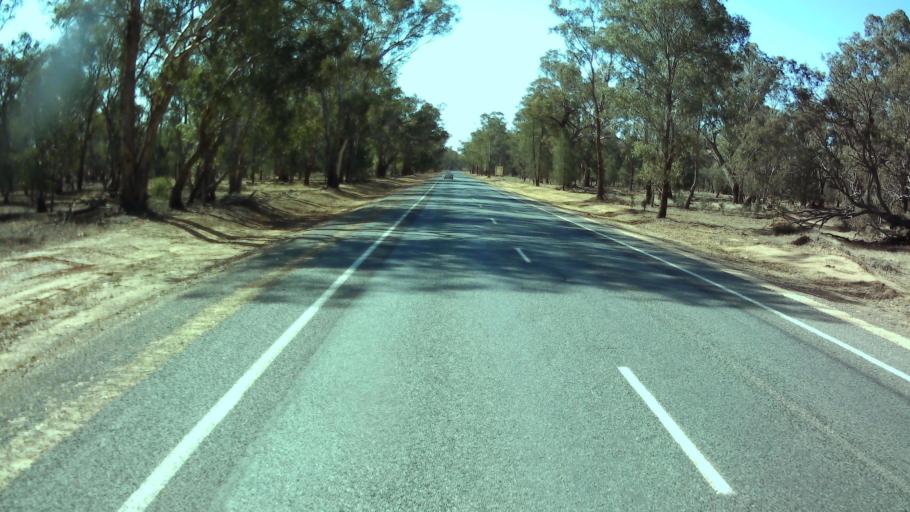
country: AU
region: New South Wales
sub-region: Weddin
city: Grenfell
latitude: -33.7254
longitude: 148.0859
